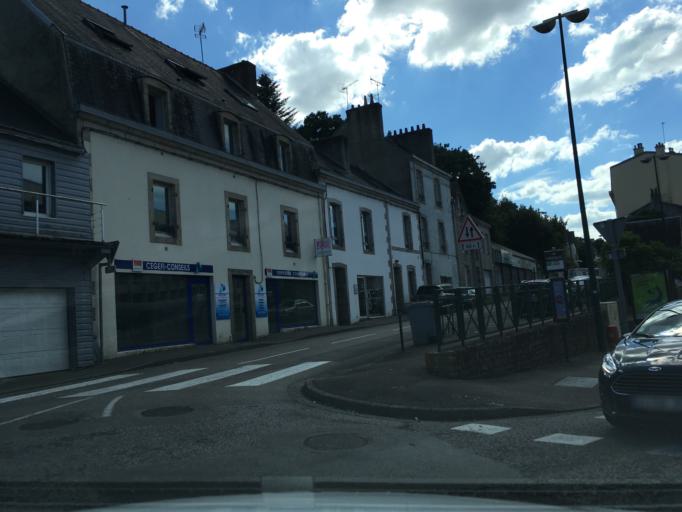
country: FR
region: Brittany
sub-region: Departement du Finistere
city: Quimper
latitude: 47.9925
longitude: -4.0820
